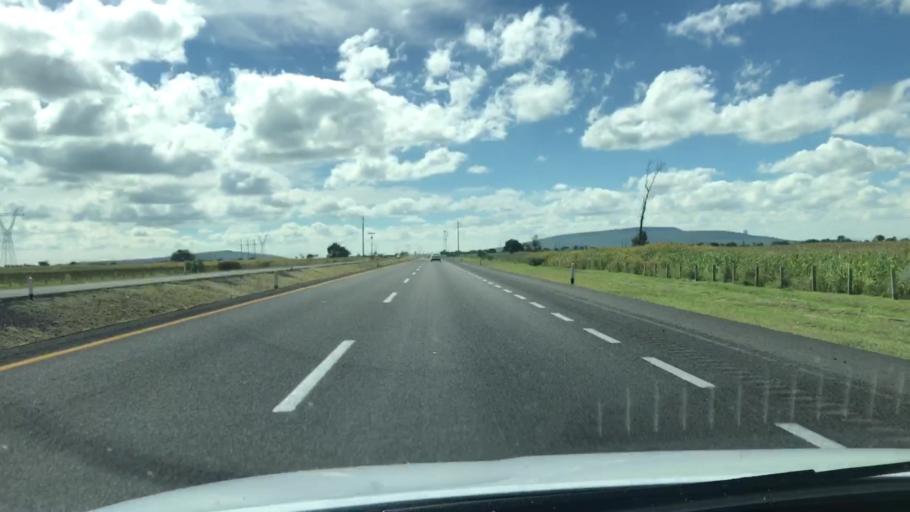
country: MX
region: Guanajuato
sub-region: Irapuato
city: Serrano
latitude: 20.8061
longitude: -101.4338
